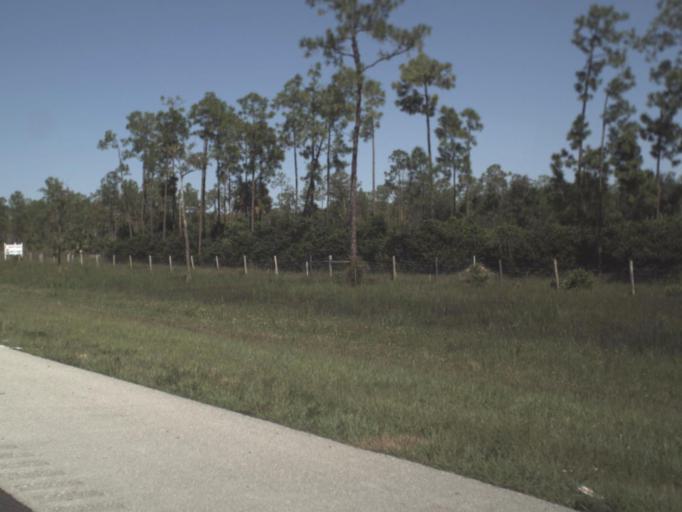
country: US
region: Florida
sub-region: Lee County
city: Bonita Springs
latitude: 26.3813
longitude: -81.7720
